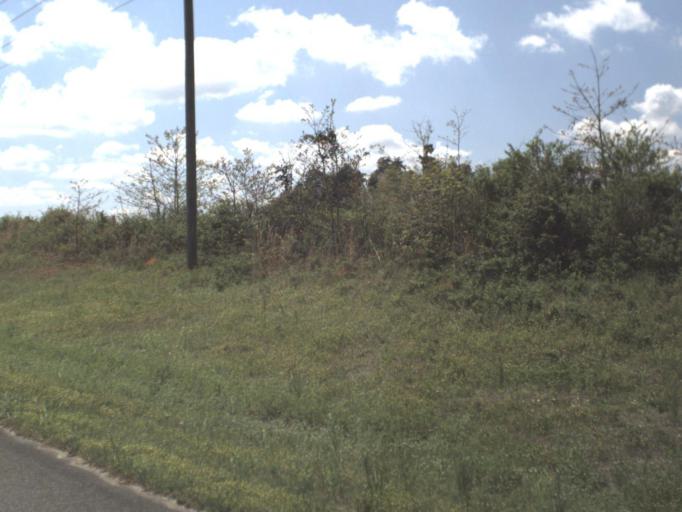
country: US
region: Florida
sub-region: Okaloosa County
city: Crestview
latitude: 30.8869
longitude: -86.6628
